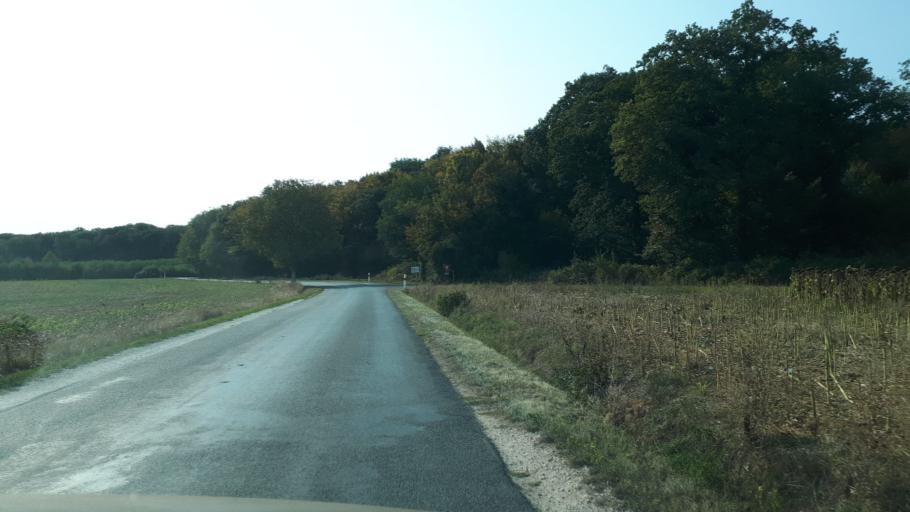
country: FR
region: Centre
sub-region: Departement du Cher
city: Rians
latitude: 47.1858
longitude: 2.6476
